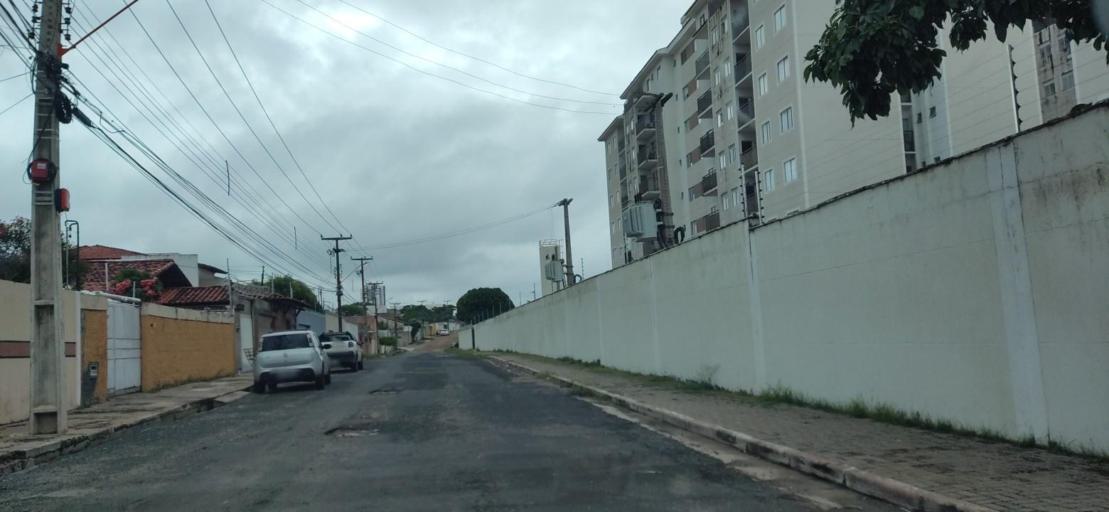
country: BR
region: Piaui
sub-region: Teresina
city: Teresina
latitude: -5.0718
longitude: -42.7573
